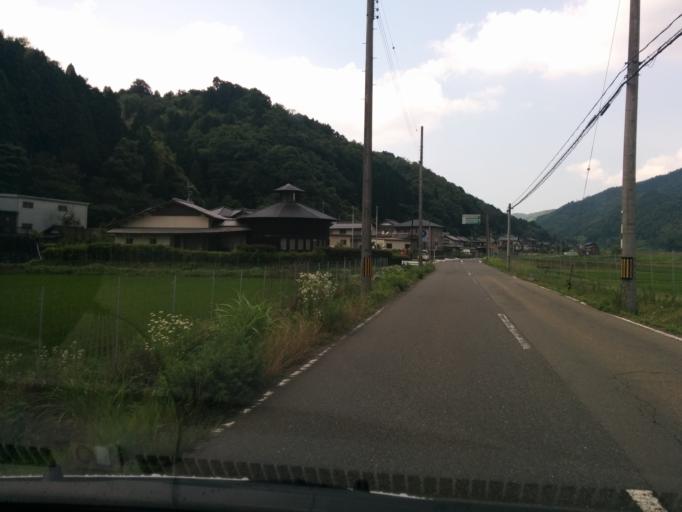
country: JP
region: Kyoto
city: Fukuchiyama
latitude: 35.4131
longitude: 135.1524
